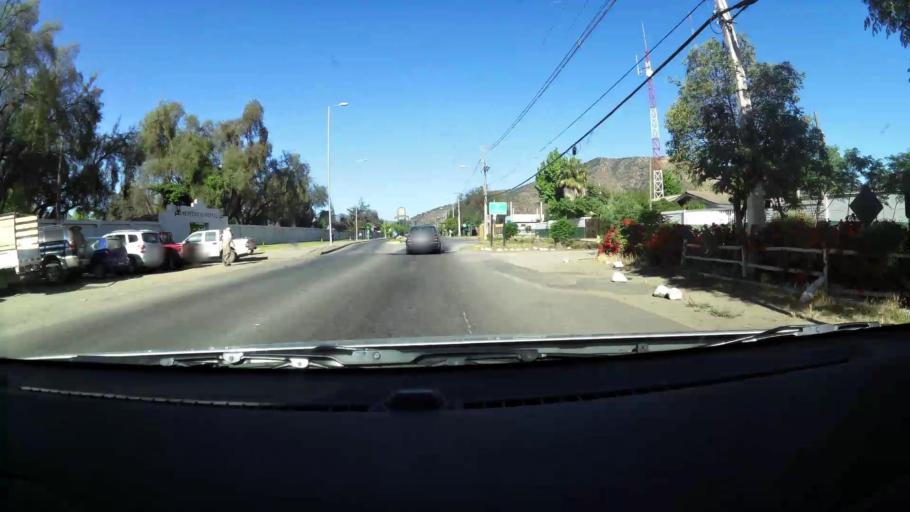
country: CL
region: Santiago Metropolitan
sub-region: Provincia de Chacabuco
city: Lampa
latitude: -33.4016
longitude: -71.1197
